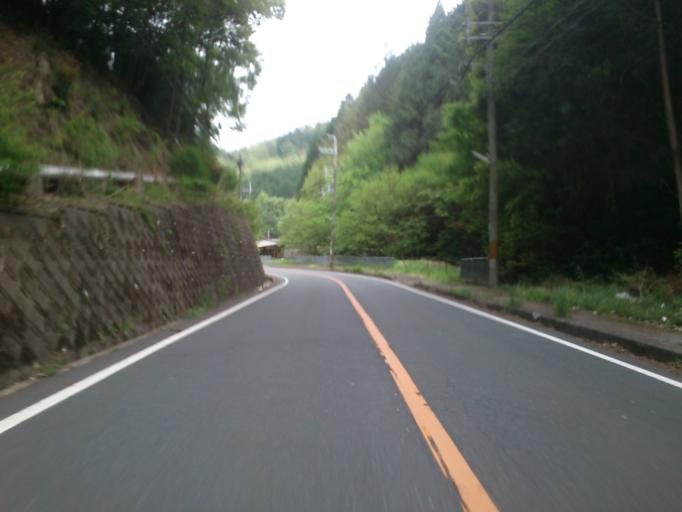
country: JP
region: Kyoto
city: Kameoka
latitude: 34.9728
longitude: 135.5152
